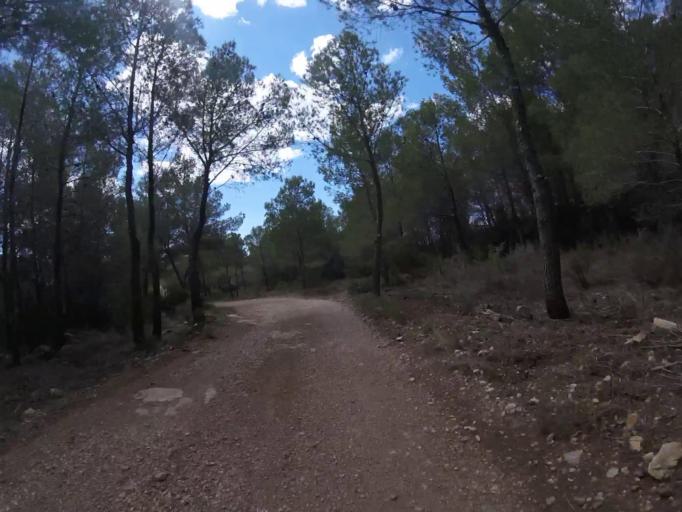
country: ES
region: Valencia
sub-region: Provincia de Castello
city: Alcoceber
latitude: 40.2919
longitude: 0.3149
